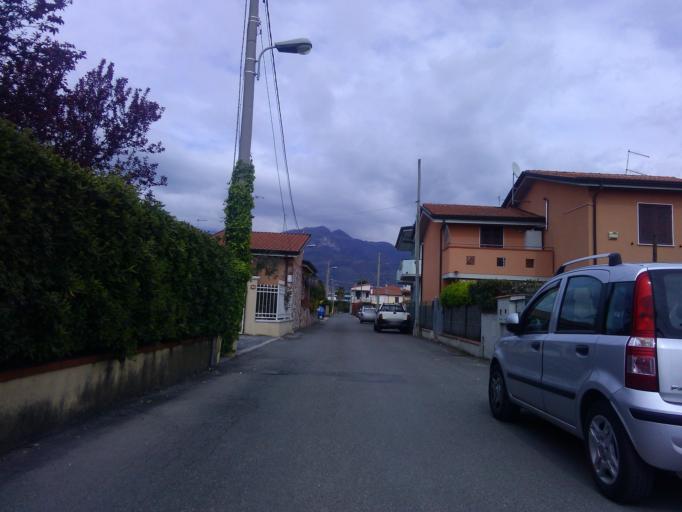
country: IT
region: Tuscany
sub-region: Provincia di Massa-Carrara
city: Massa
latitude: 44.0228
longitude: 10.0946
